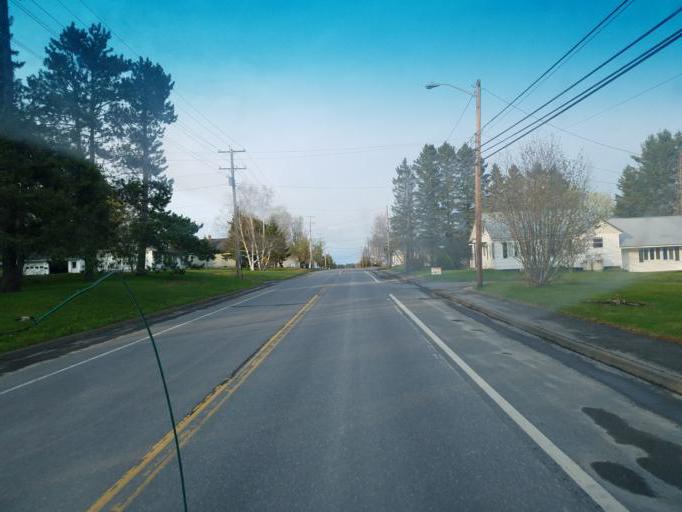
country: US
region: Maine
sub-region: Aroostook County
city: Caribou
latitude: 46.8557
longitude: -68.0262
